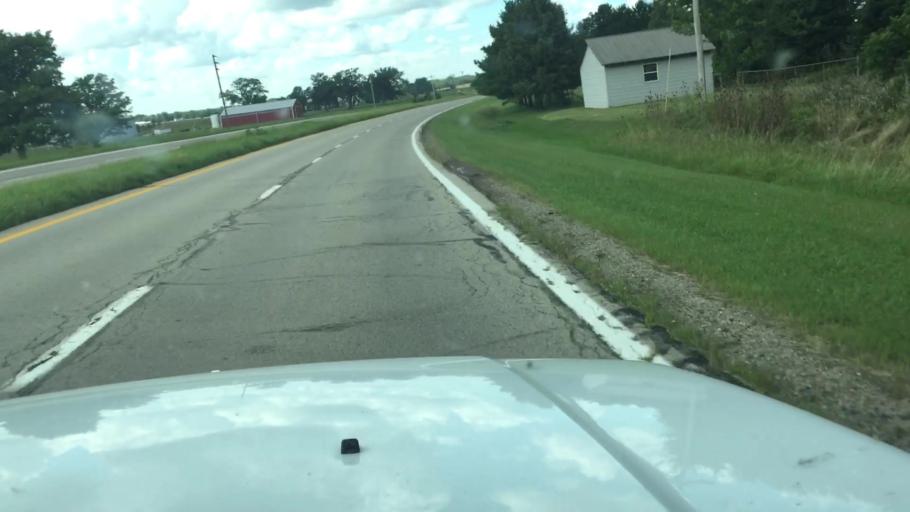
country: US
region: Ohio
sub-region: Madison County
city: Choctaw Lake
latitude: 39.9328
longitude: -83.4955
